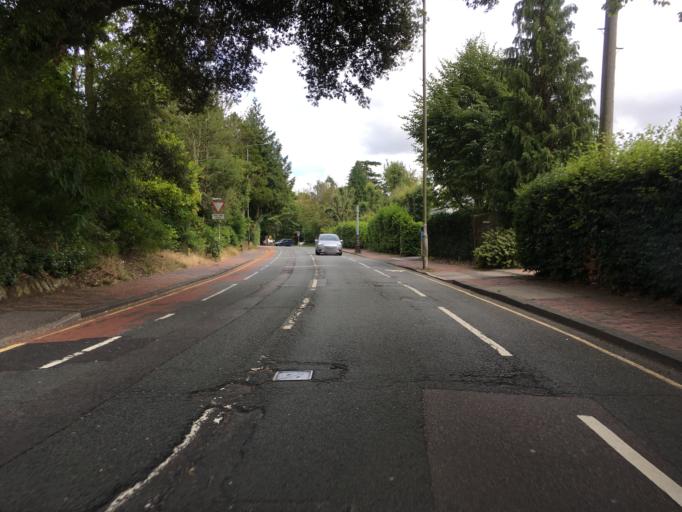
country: GB
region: England
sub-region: Kent
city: Royal Tunbridge Wells
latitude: 51.1327
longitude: 0.2737
